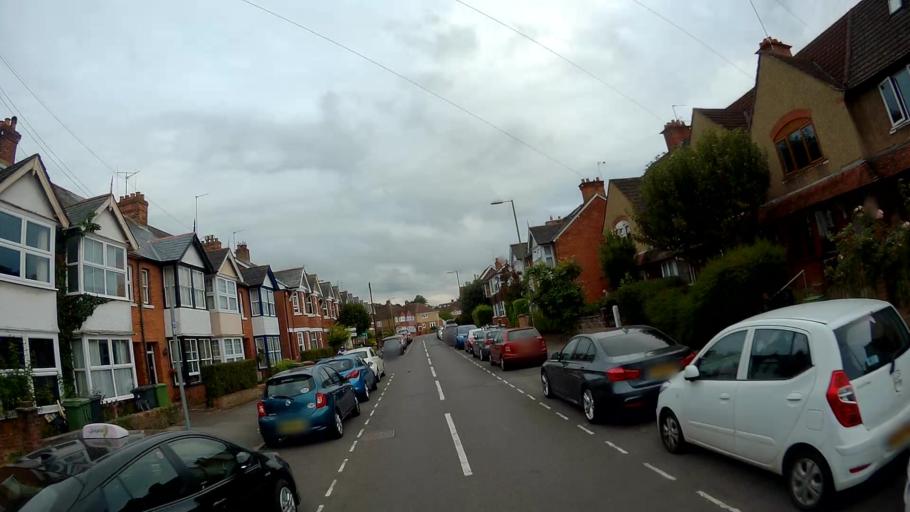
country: GB
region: England
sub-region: Hampshire
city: Basingstoke
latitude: 51.2630
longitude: -1.0943
